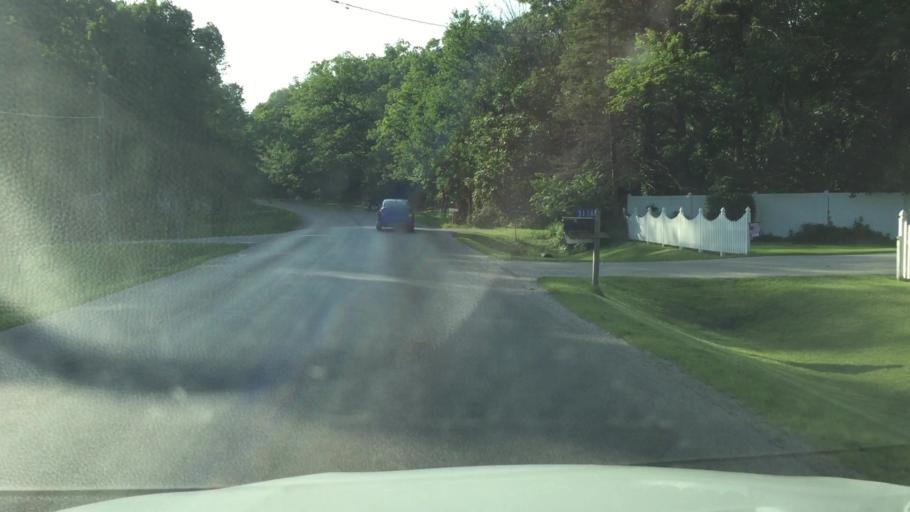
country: US
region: Iowa
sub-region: Linn County
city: Ely
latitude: 41.8291
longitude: -91.6263
